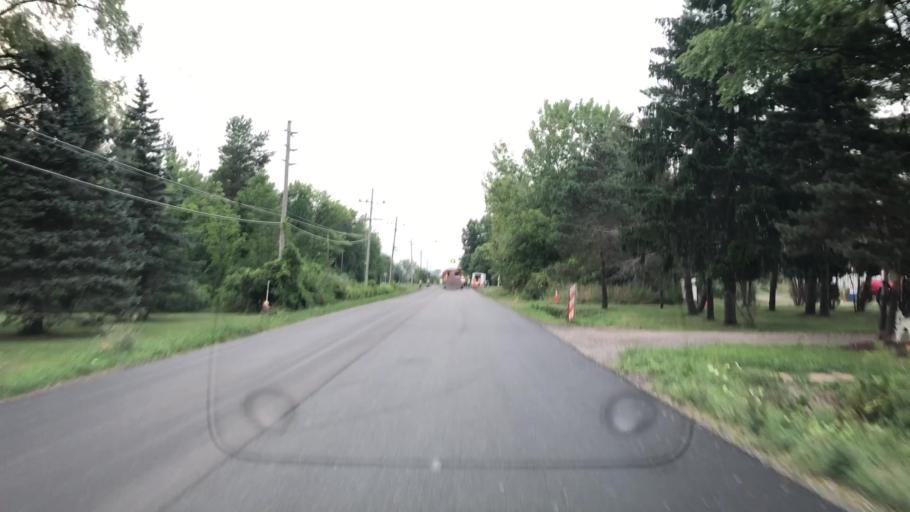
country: US
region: New York
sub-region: Erie County
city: Elma Center
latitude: 42.8211
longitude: -78.6059
